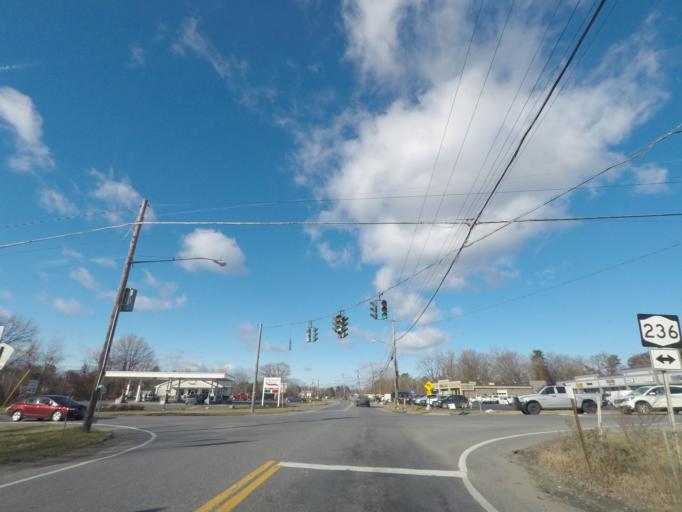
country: US
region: New York
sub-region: Saratoga County
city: Waterford
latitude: 42.8374
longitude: -73.7382
